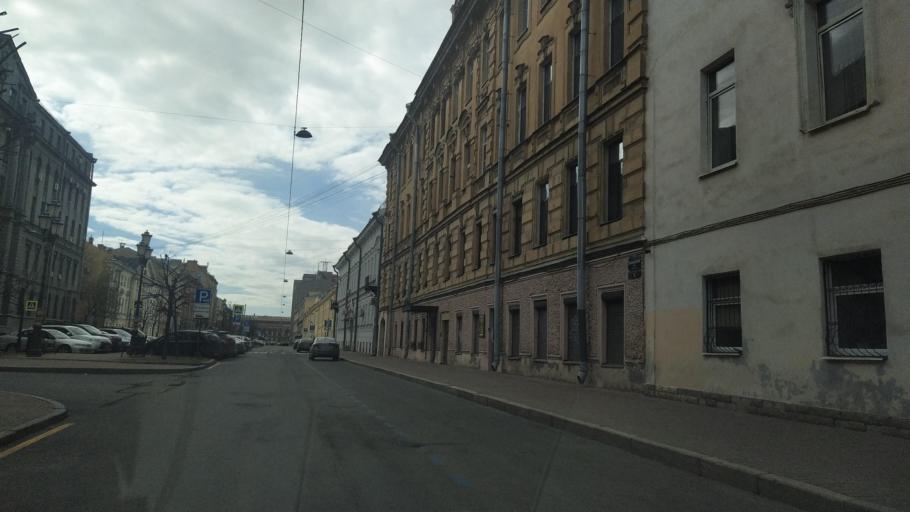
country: RU
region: St.-Petersburg
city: Centralniy
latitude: 59.9479
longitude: 30.3573
